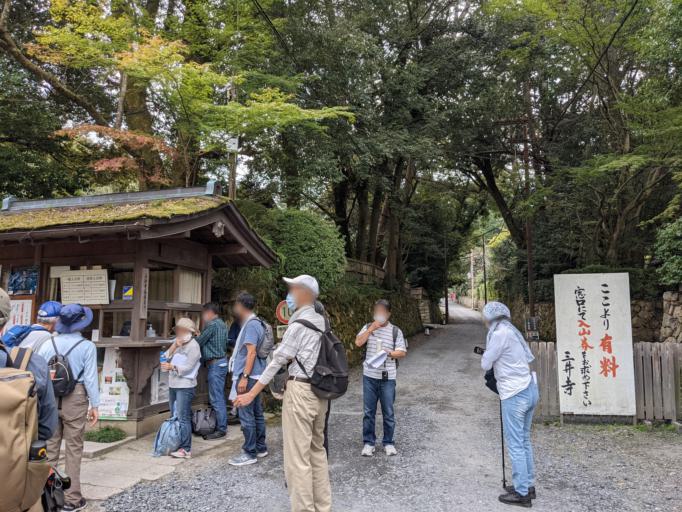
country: JP
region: Shiga Prefecture
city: Otsu-shi
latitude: 35.0118
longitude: 135.8549
